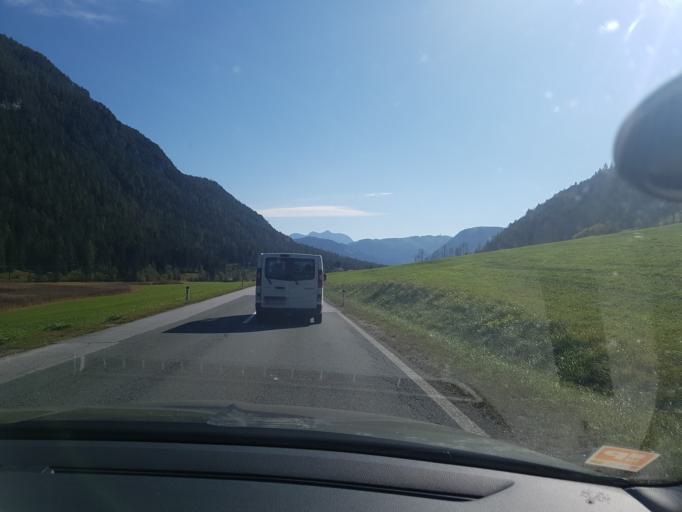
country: AT
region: Tyrol
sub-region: Politischer Bezirk Kitzbuhel
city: Waidring
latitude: 47.5535
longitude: 12.5668
